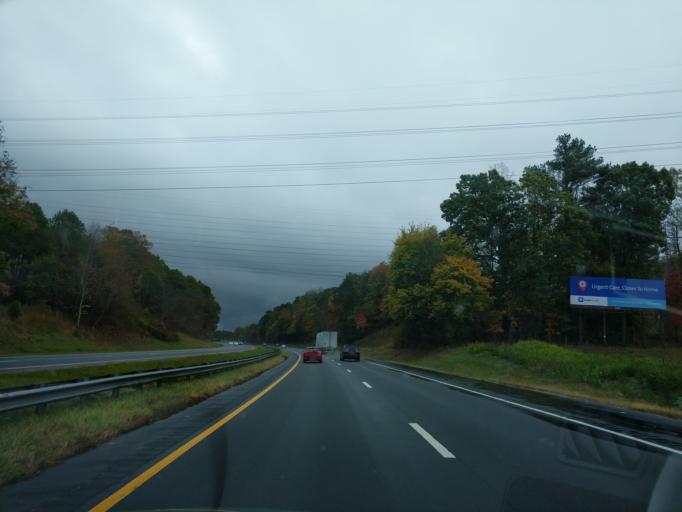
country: US
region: North Carolina
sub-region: Orange County
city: Hillsborough
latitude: 36.0396
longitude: -79.0260
